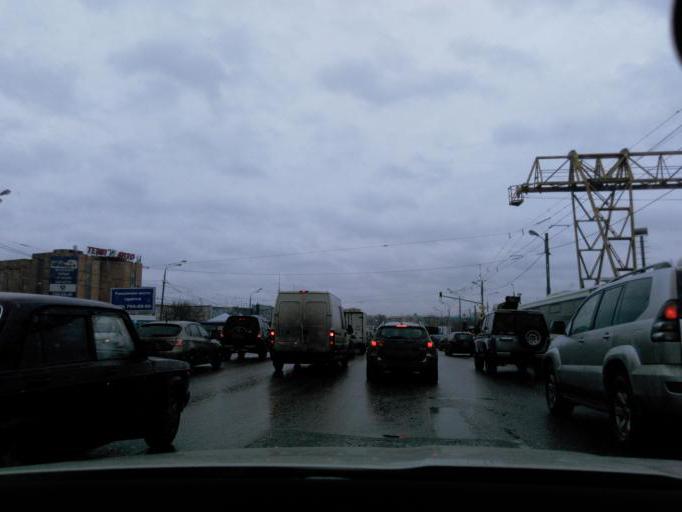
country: RU
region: Moscow
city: Likhobory
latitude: 55.8553
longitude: 37.5619
